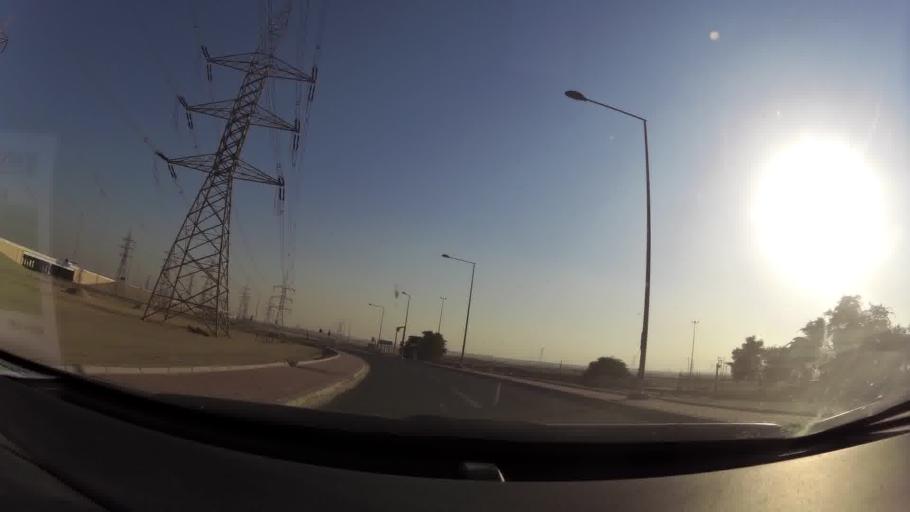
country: KW
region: Al Ahmadi
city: Al Fahahil
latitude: 29.0470
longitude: 48.1116
